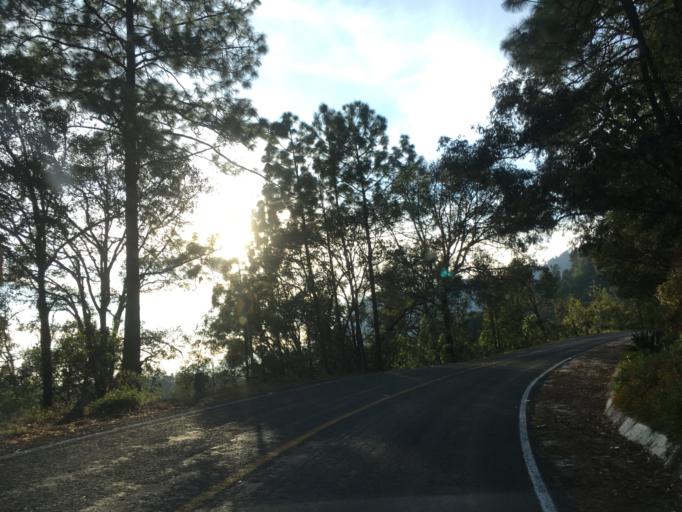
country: MX
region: Michoacan
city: Tzitzio
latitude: 19.6676
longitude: -100.9053
